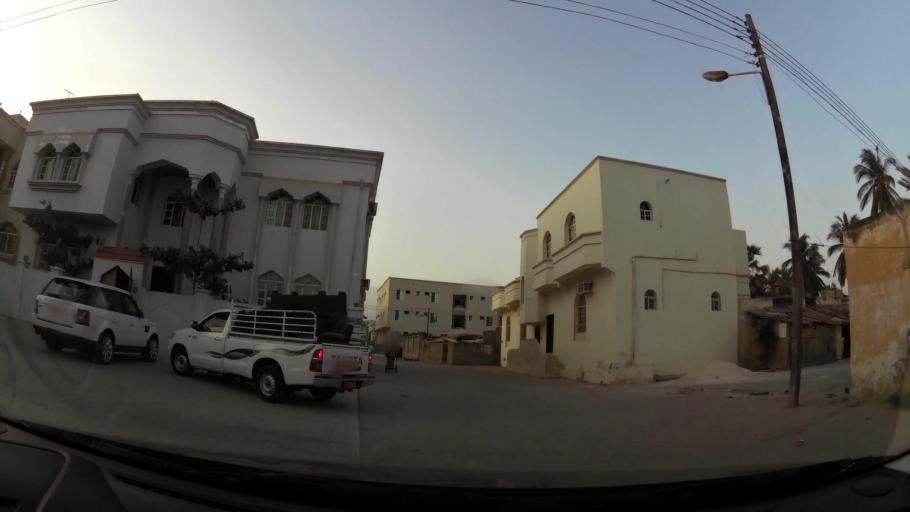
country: OM
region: Zufar
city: Salalah
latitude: 17.0197
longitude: 54.1255
